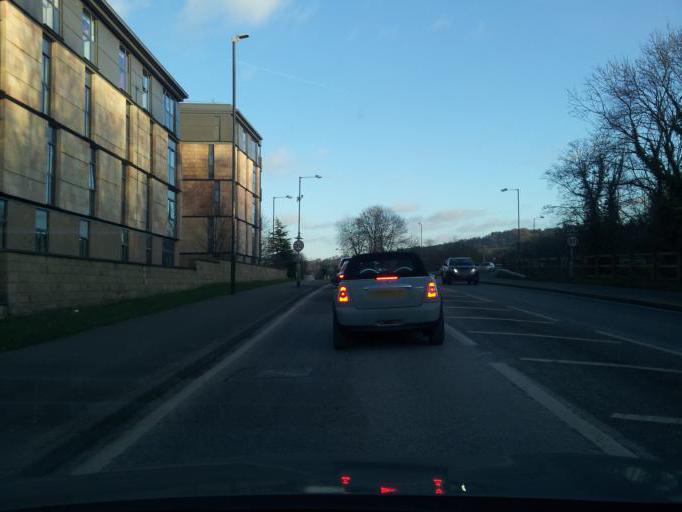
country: GB
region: England
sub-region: Derbyshire
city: Matlock
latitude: 53.1415
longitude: -1.5659
